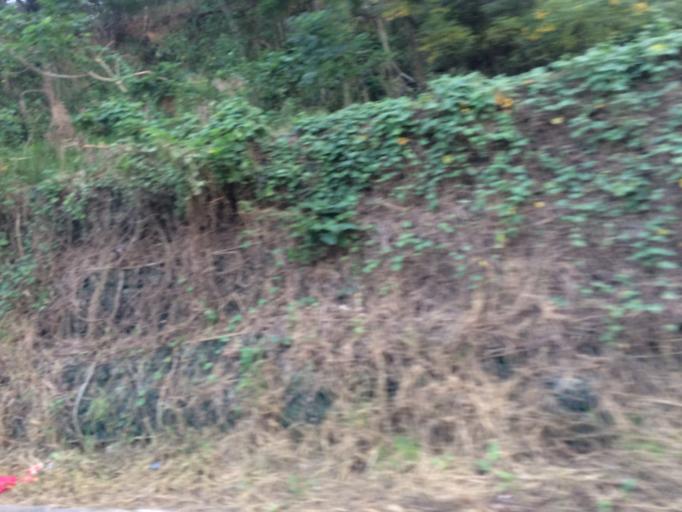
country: TW
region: Taiwan
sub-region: Hsinchu
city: Hsinchu
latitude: 24.7170
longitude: 120.9160
